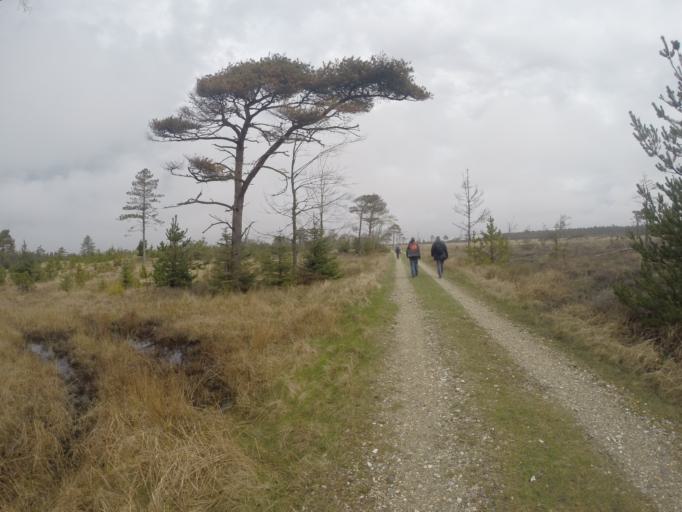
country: DK
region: North Denmark
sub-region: Thisted Kommune
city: Hanstholm
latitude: 57.0395
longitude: 8.5578
